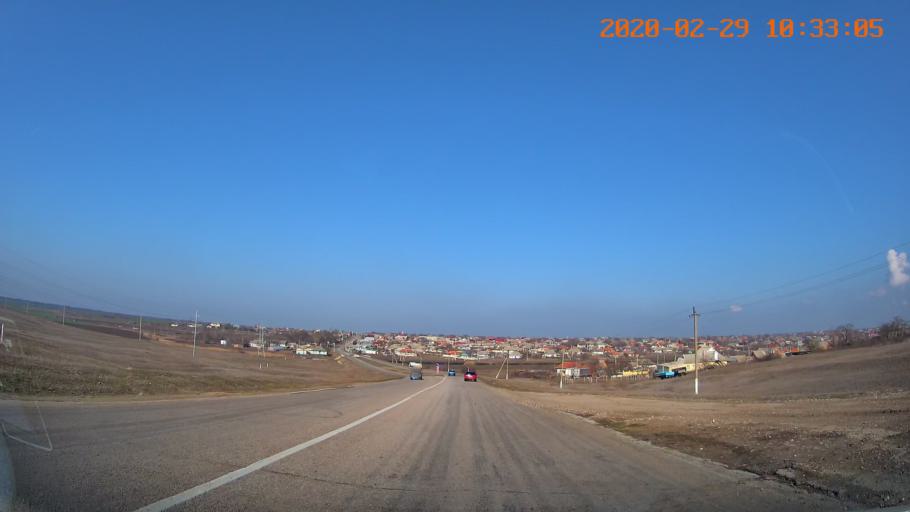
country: UA
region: Odessa
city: Velykoploske
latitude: 46.9682
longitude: 29.5485
